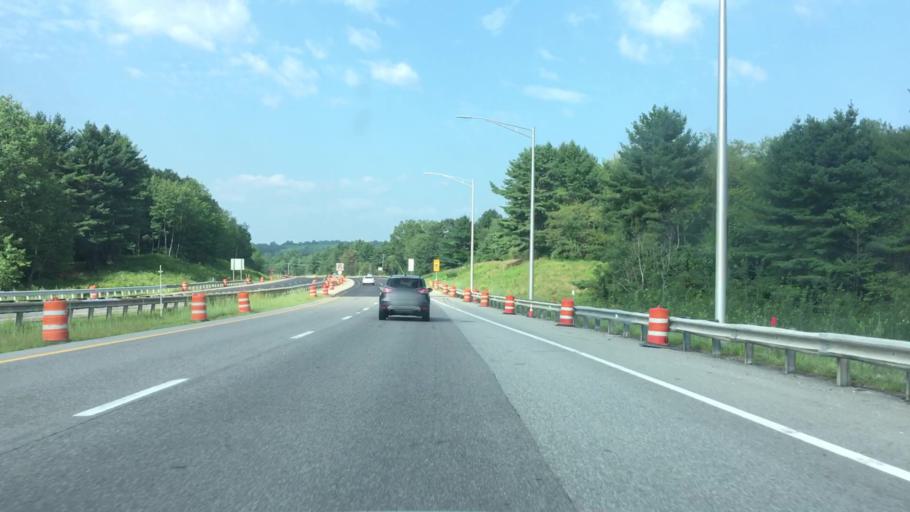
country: US
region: Maine
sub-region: Androscoggin County
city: Lewiston
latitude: 44.0722
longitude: -70.1924
